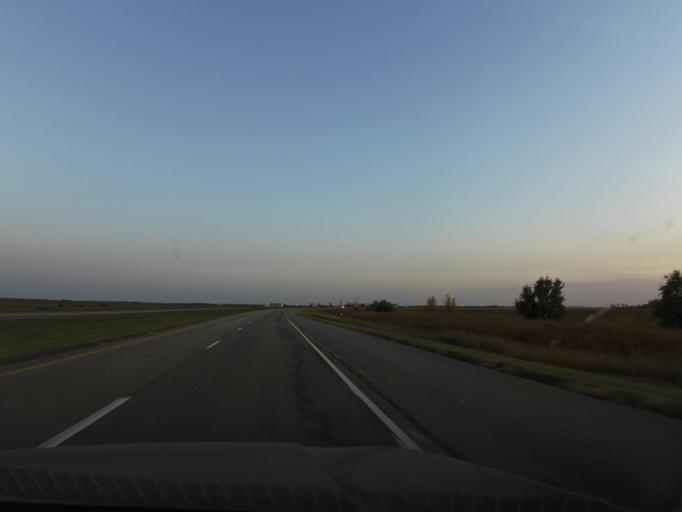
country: US
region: Minnesota
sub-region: Kittson County
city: Hallock
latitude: 48.6248
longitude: -97.1818
